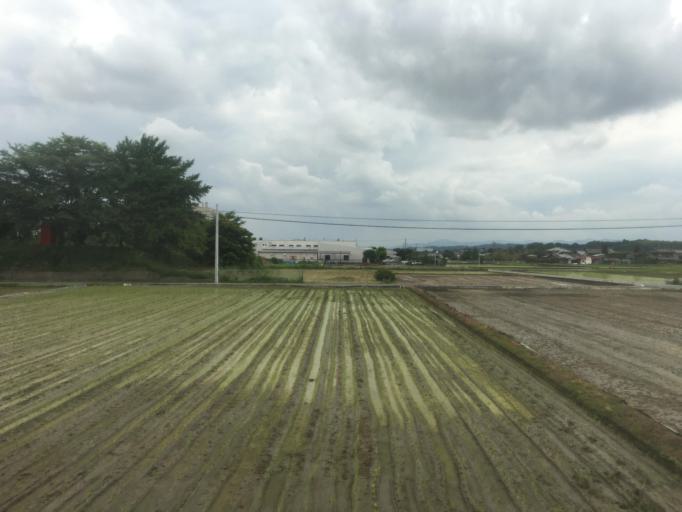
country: JP
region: Gunma
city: Fujioka
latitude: 36.2731
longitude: 139.0350
